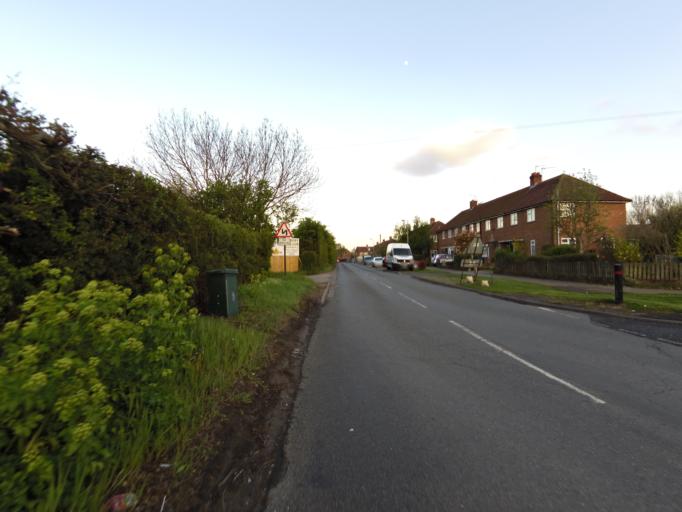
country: GB
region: England
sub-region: Suffolk
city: Ipswich
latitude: 52.0734
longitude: 1.1897
